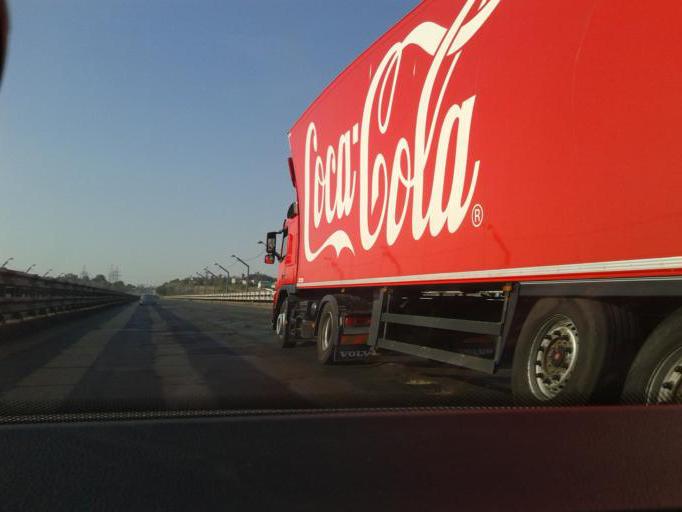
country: RU
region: Volgograd
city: Volgograd
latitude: 48.7180
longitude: 44.4446
